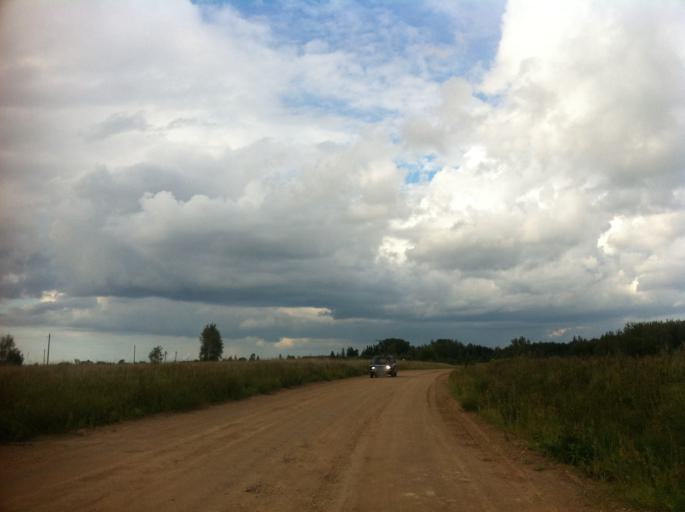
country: RU
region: Pskov
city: Izborsk
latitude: 57.8324
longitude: 27.9835
